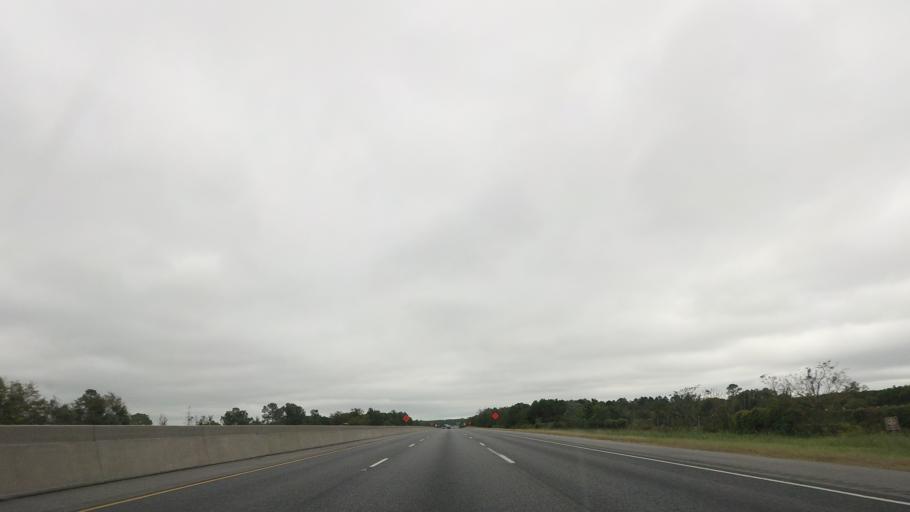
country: US
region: Georgia
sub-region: Tift County
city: Tifton
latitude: 31.5275
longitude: -83.5224
